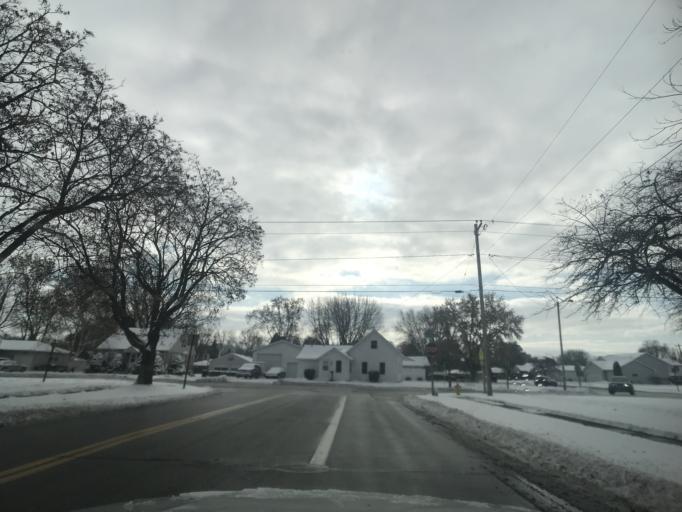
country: US
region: Wisconsin
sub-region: Brown County
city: De Pere
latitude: 44.4454
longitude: -88.0856
